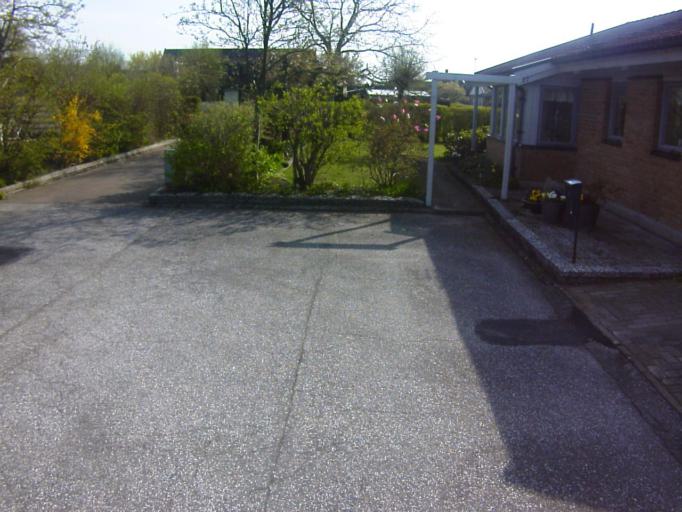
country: SE
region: Skane
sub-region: Kavlinge Kommun
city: Loddekopinge
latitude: 55.7645
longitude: 13.0041
